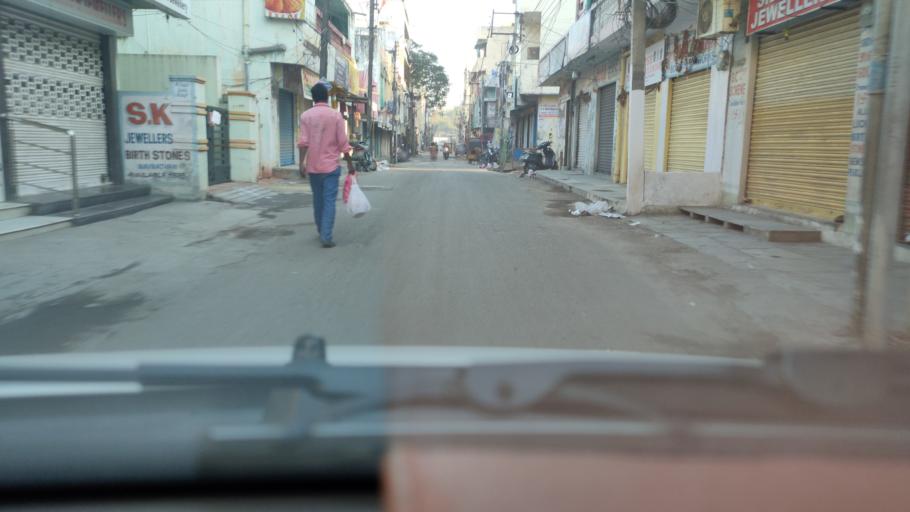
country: IN
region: Telangana
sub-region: Hyderabad
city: Malkajgiri
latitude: 17.4122
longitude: 78.5086
